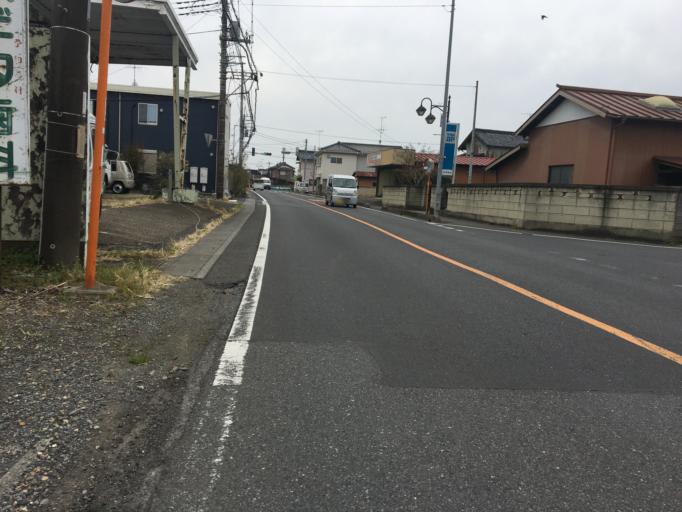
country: JP
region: Saitama
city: Kazo
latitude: 36.1125
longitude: 139.5927
